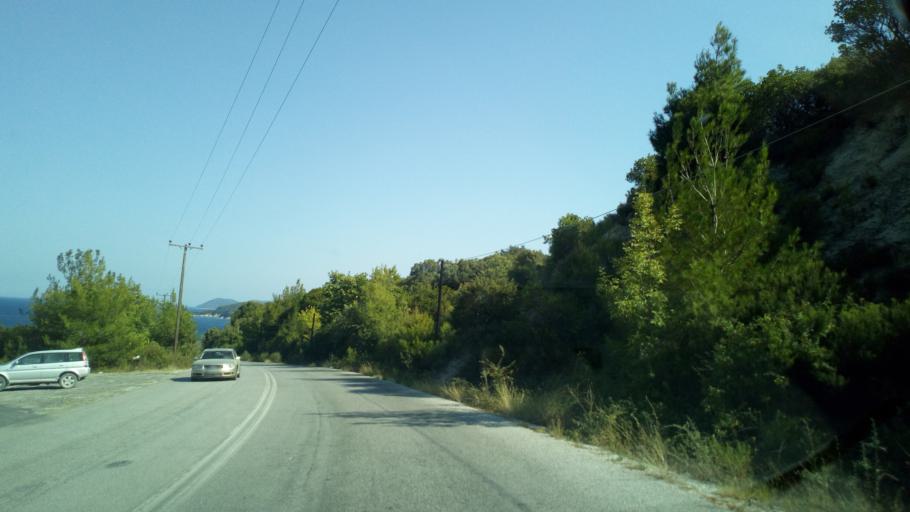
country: GR
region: Central Macedonia
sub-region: Nomos Chalkidikis
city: Stratonion
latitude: 40.5886
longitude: 23.7926
